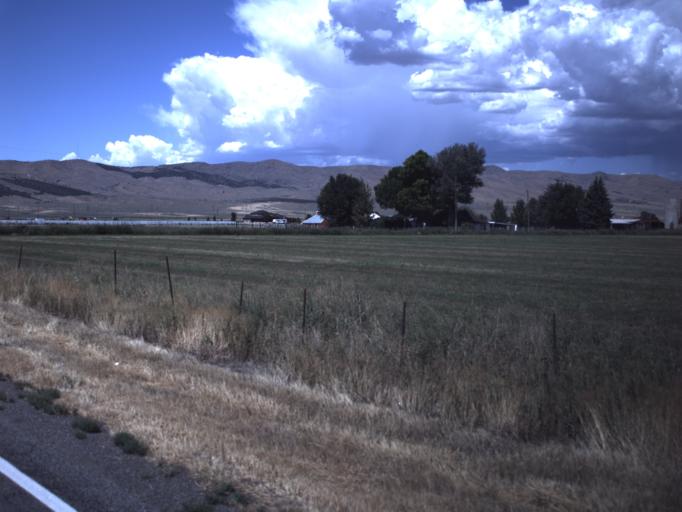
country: US
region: Utah
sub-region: Juab County
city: Nephi
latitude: 39.7101
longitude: -111.8690
